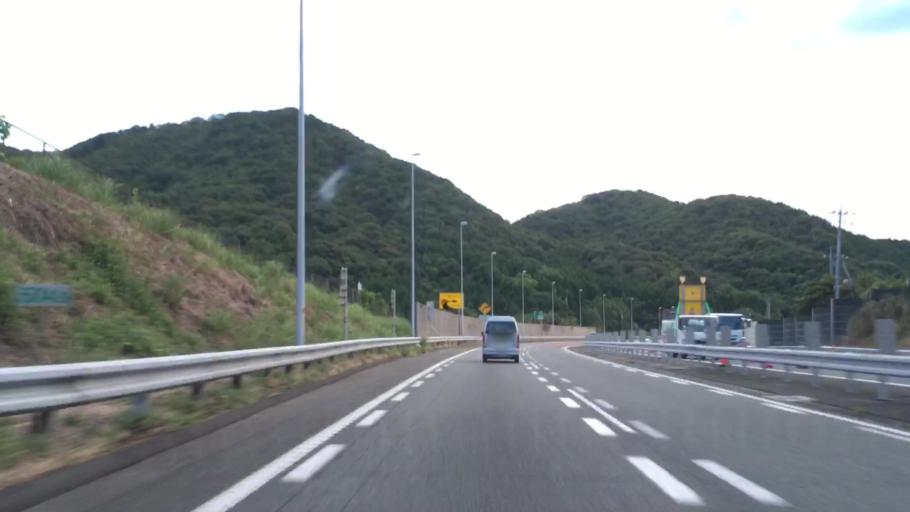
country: JP
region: Yamaguchi
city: Onoda
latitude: 34.1213
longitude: 131.2111
